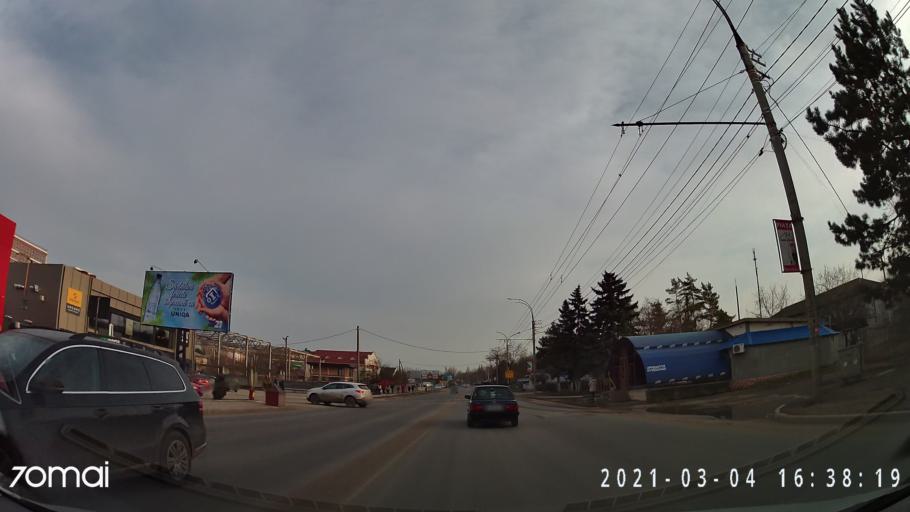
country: MD
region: Balti
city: Balti
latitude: 47.7815
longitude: 27.8903
